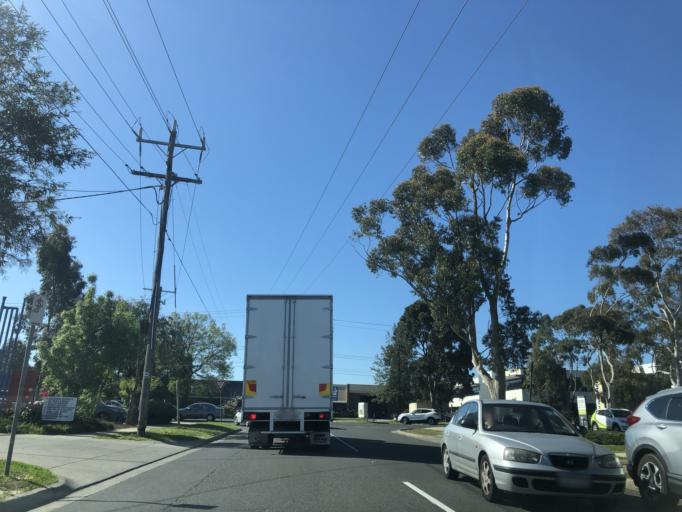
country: AU
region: Victoria
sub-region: Monash
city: Notting Hill
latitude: -37.9013
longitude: 145.1381
